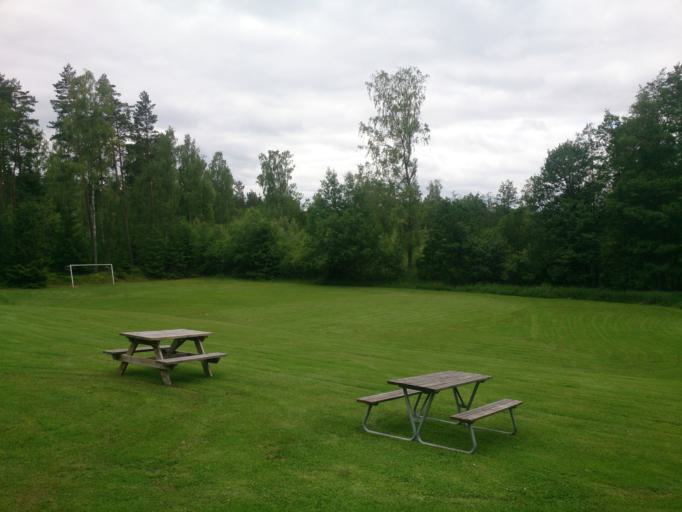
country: SE
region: OEstergoetland
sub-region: Atvidabergs Kommun
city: Atvidaberg
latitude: 58.2103
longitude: 15.9996
